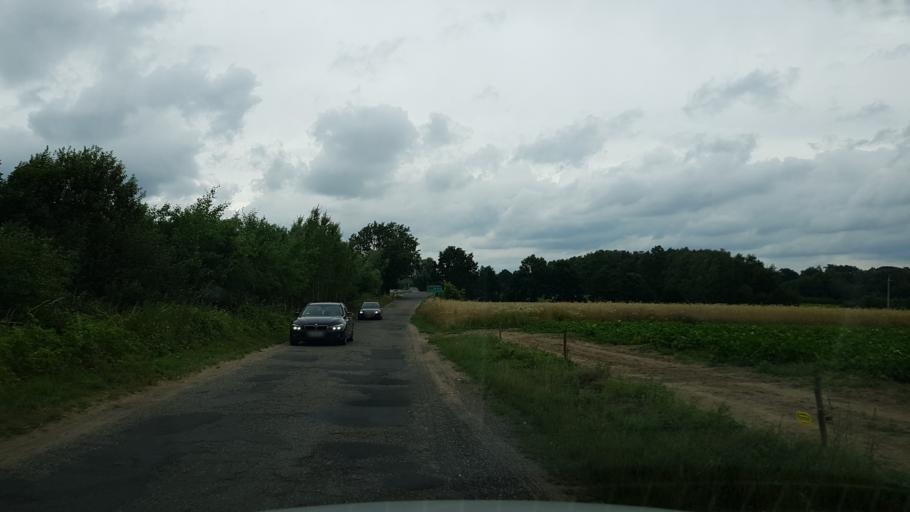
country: PL
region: West Pomeranian Voivodeship
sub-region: Powiat goleniowski
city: Maszewo
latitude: 53.4273
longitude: 14.9982
